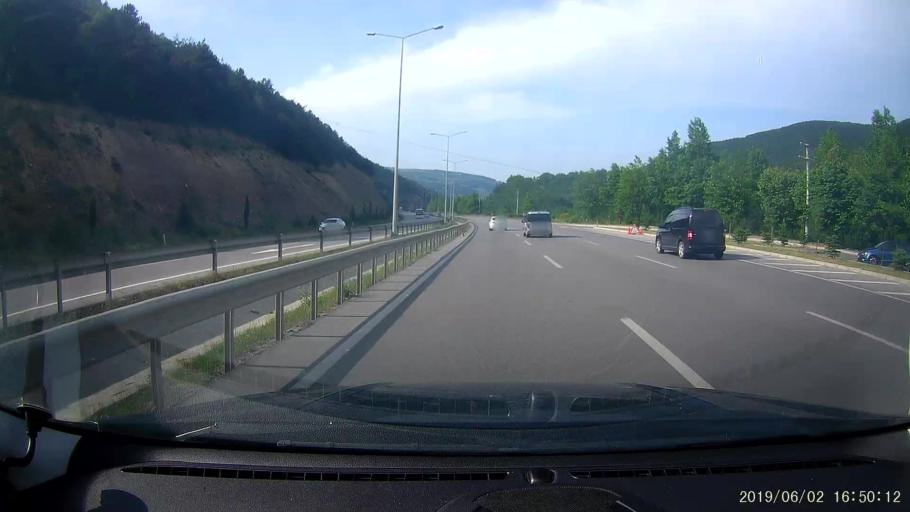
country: TR
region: Samsun
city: Samsun
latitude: 41.2500
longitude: 36.1734
